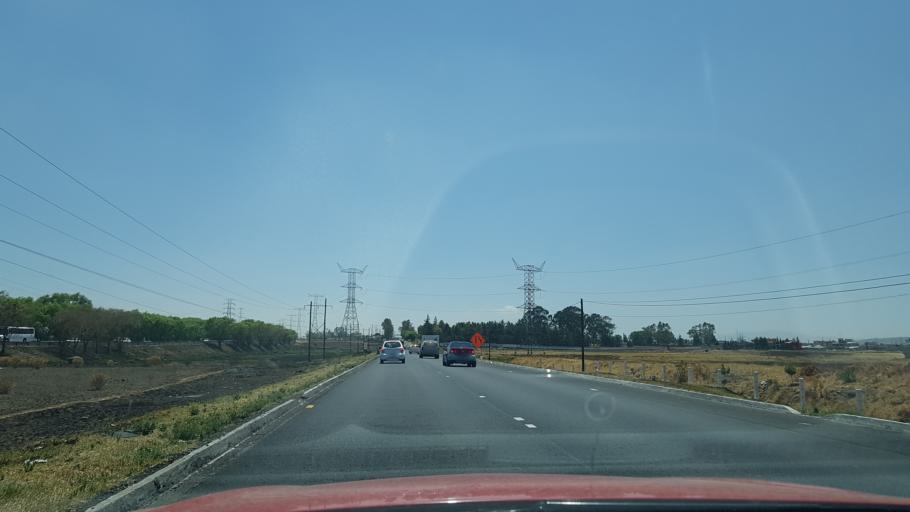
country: MX
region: Mexico
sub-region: Ixtlahuaca
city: Santo Domingo de Guzman
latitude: 19.6052
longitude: -99.7744
